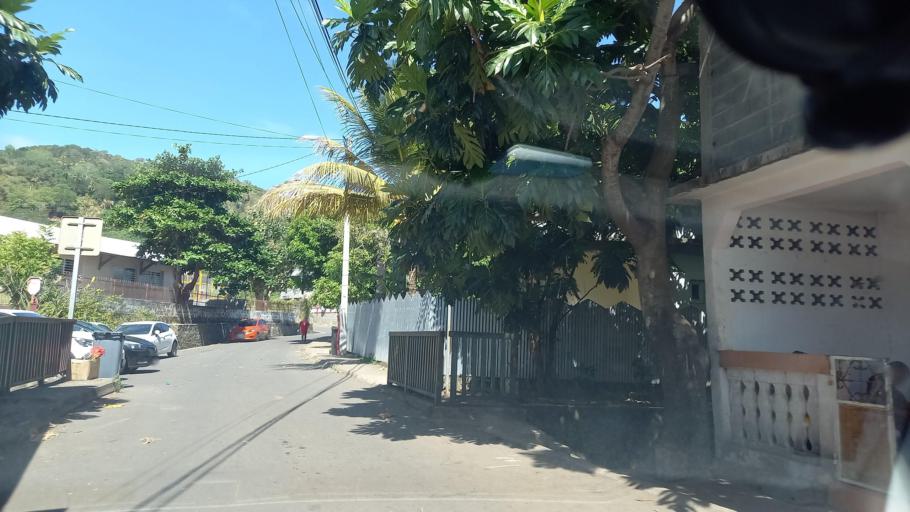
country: YT
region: Kani-Keli
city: Kani Keli
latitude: -12.9649
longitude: 45.1112
